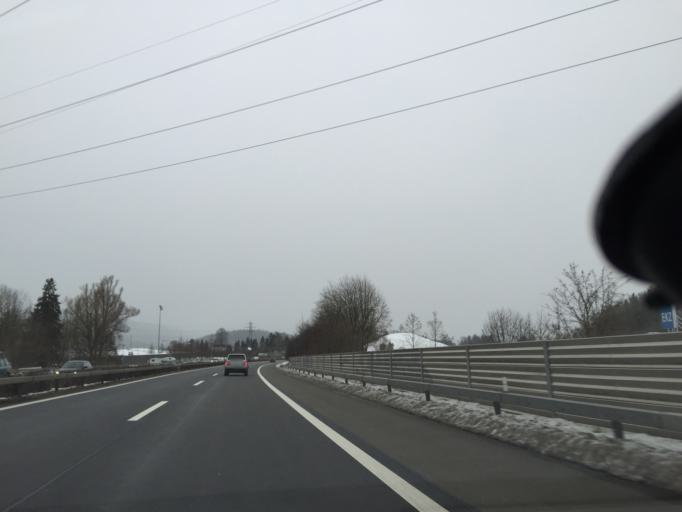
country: CH
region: Zurich
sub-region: Bezirk Horgen
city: Thalwil / Berg
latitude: 47.2873
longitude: 8.5541
